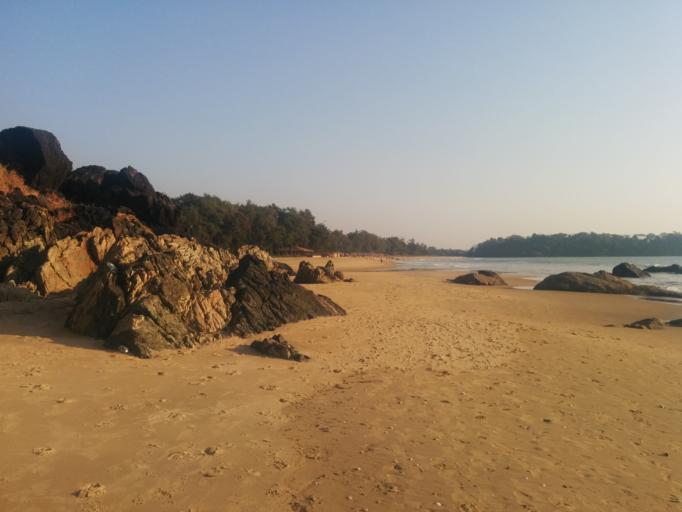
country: IN
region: Karnataka
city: Canacona
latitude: 14.9939
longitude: 74.0349
